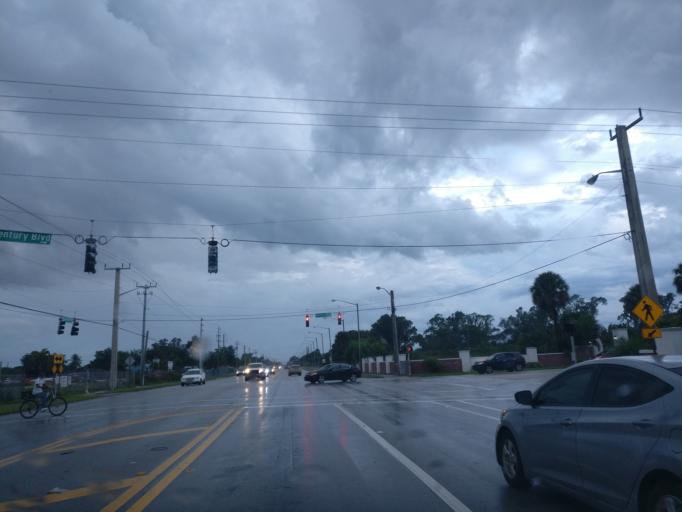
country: US
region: Florida
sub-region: Palm Beach County
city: Schall Circle
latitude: 26.7154
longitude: -80.1191
